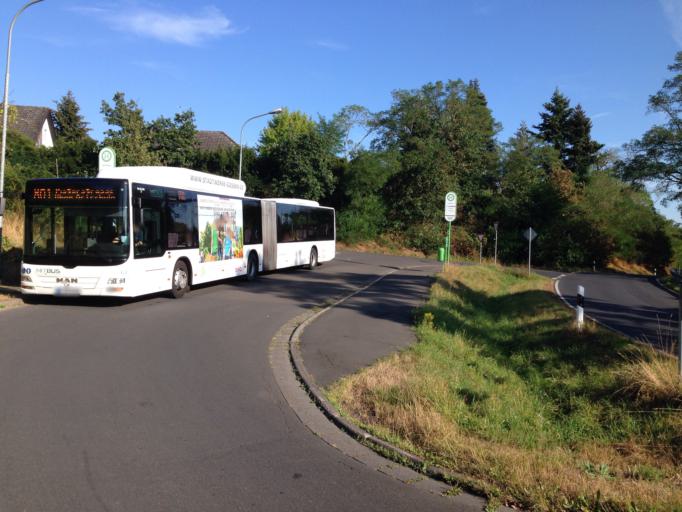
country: DE
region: Hesse
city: Lollar
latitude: 50.6391
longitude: 8.6614
